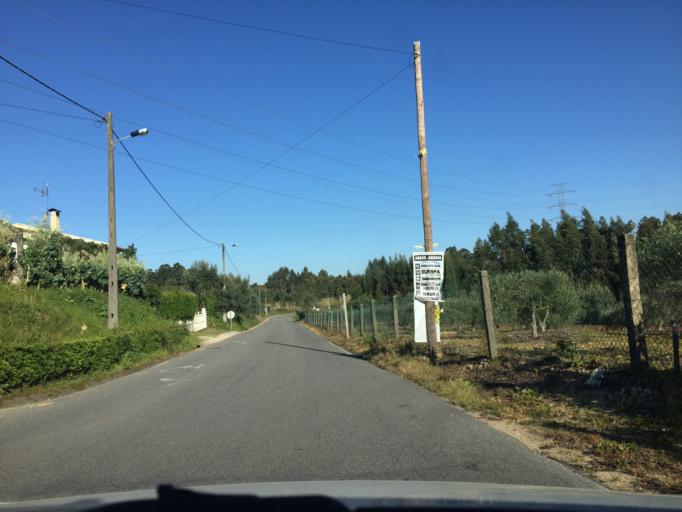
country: PT
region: Aveiro
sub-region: Anadia
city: Sangalhos
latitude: 40.4530
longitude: -8.4830
